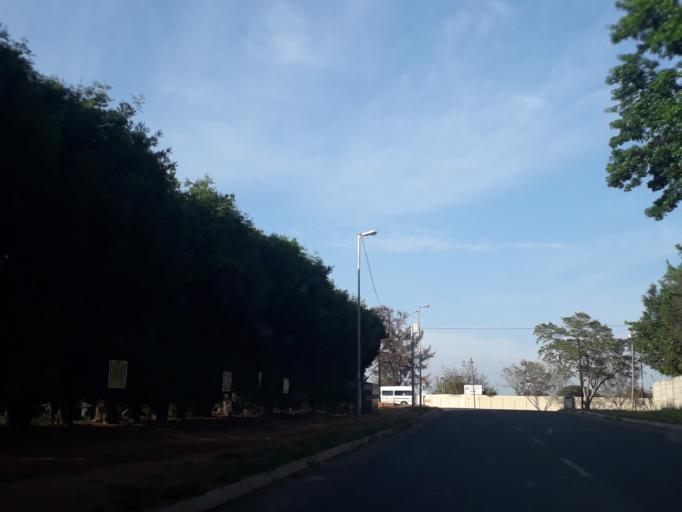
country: ZA
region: Gauteng
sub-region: City of Johannesburg Metropolitan Municipality
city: Roodepoort
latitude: -26.0919
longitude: 27.9007
